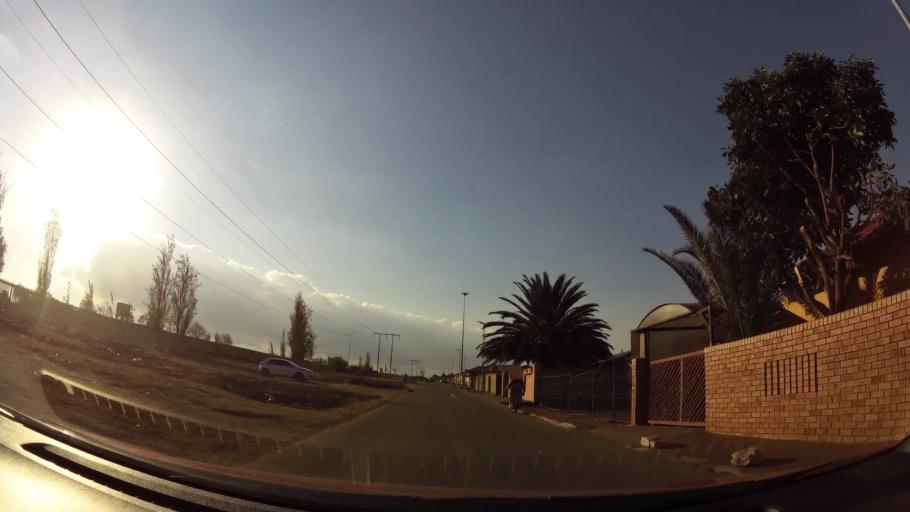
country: ZA
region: Gauteng
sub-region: City of Johannesburg Metropolitan Municipality
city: Soweto
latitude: -26.2353
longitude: 27.8588
